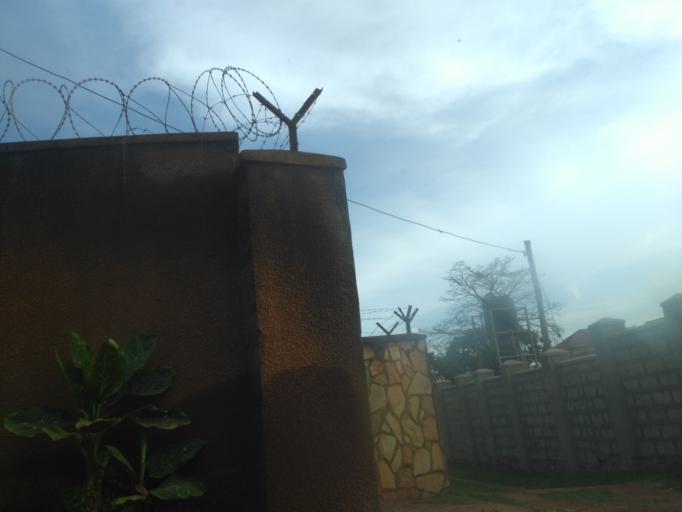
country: UG
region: Central Region
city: Kampala Central Division
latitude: 0.3479
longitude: 32.5961
